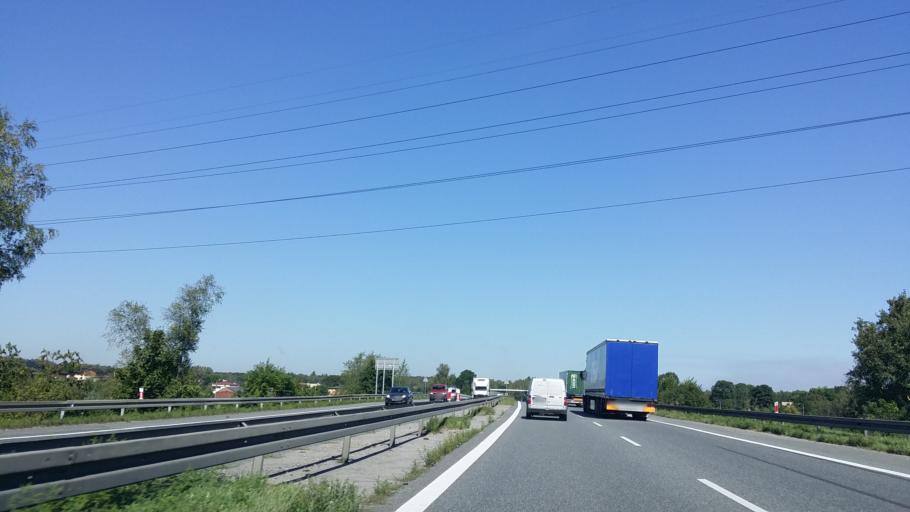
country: PL
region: Silesian Voivodeship
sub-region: Myslowice
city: Myslowice
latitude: 50.2004
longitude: 19.1684
